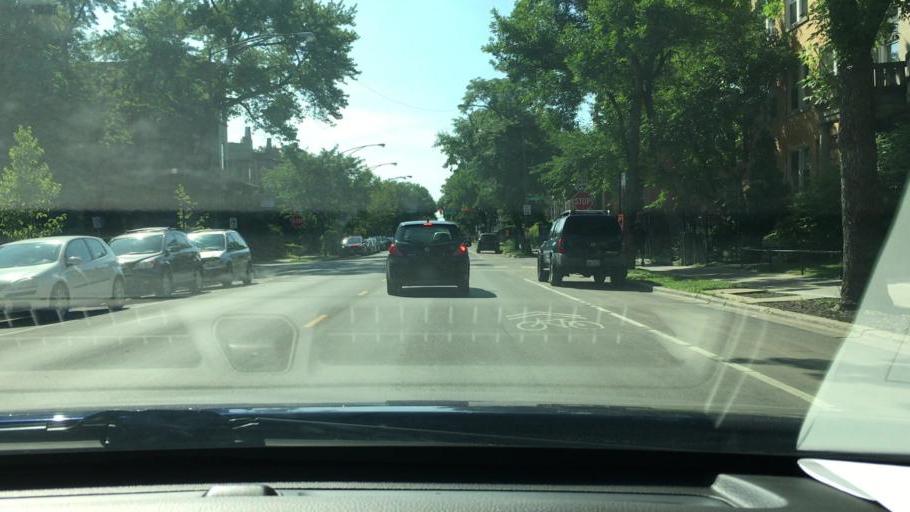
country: US
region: Illinois
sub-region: Cook County
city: Lincolnwood
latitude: 41.9284
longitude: -87.7104
